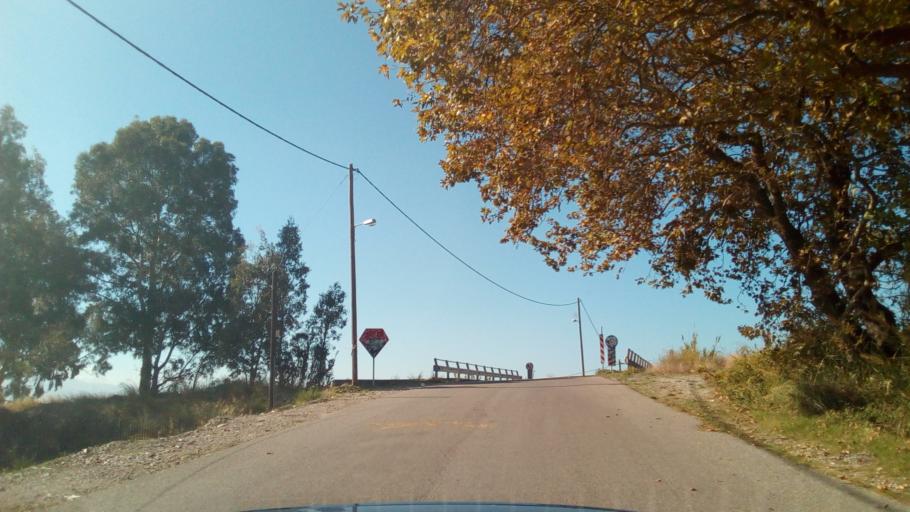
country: GR
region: West Greece
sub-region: Nomos Aitolias kai Akarnanias
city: Nafpaktos
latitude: 38.3832
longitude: 21.8182
